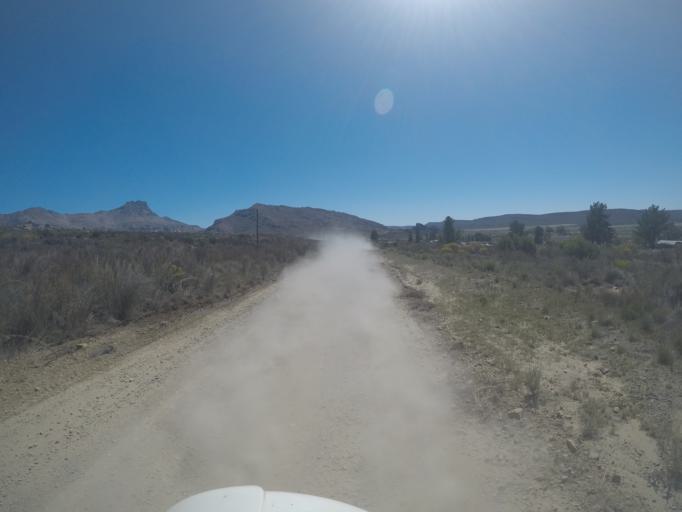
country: ZA
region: Western Cape
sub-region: Cape Winelands District Municipality
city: Ceres
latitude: -32.8701
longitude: 19.4438
